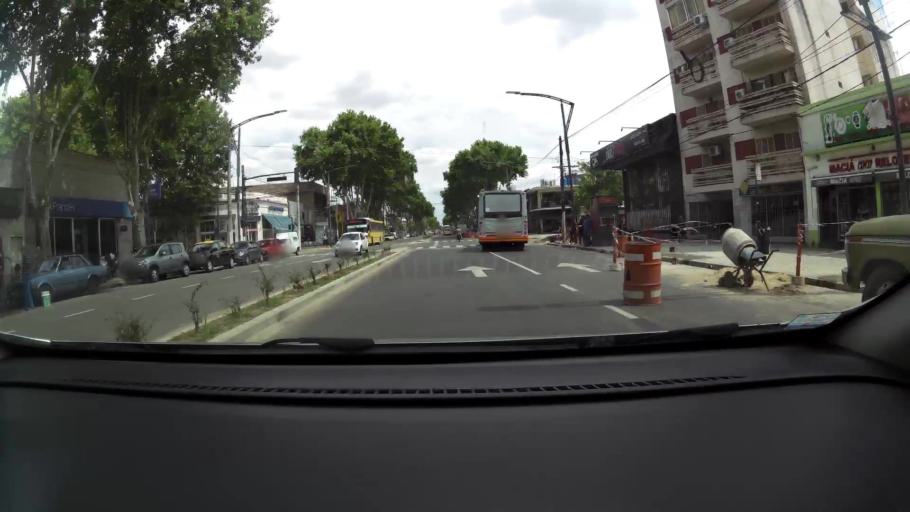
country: AR
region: Santa Fe
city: Gobernador Galvez
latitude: -32.9968
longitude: -60.6481
